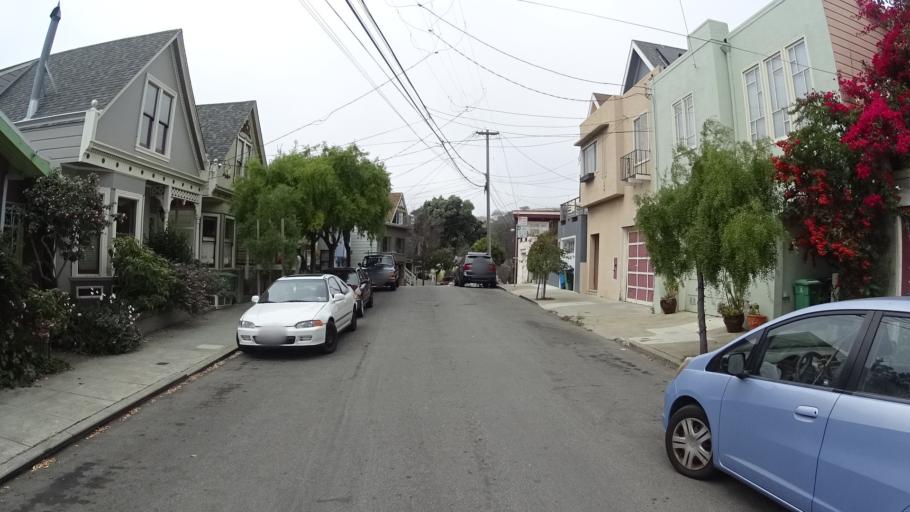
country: US
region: California
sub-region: San Mateo County
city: Daly City
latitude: 37.7359
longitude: -122.4359
